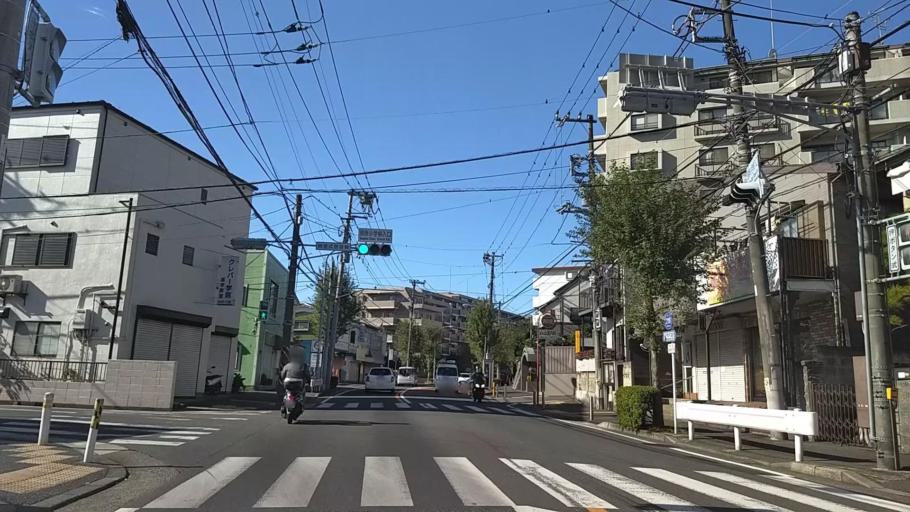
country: JP
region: Kanagawa
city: Yokohama
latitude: 35.4233
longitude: 139.5879
